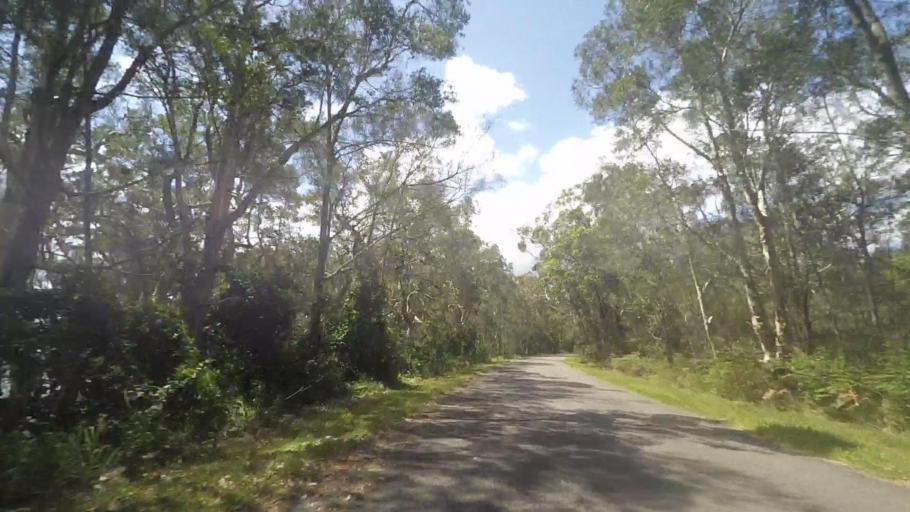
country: AU
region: New South Wales
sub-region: Great Lakes
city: Bulahdelah
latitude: -32.5186
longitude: 152.3221
